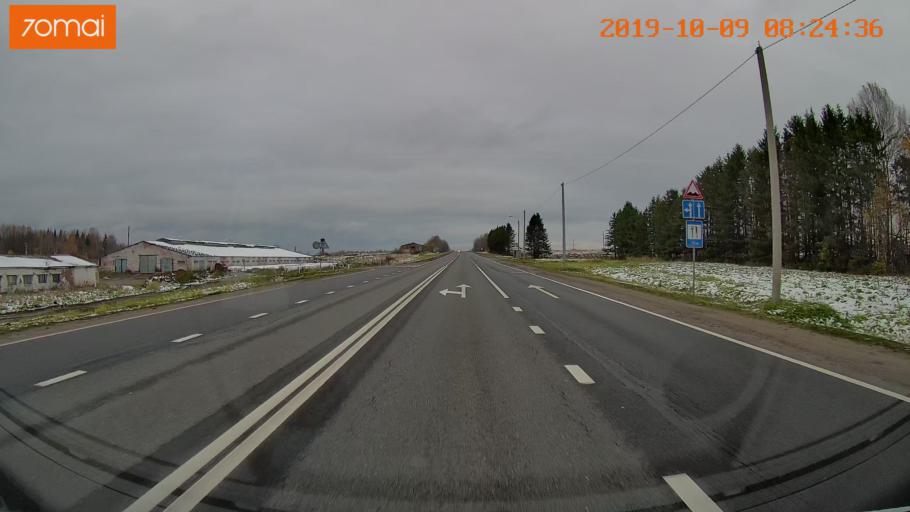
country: RU
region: Vologda
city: Gryazovets
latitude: 58.7686
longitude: 40.2775
